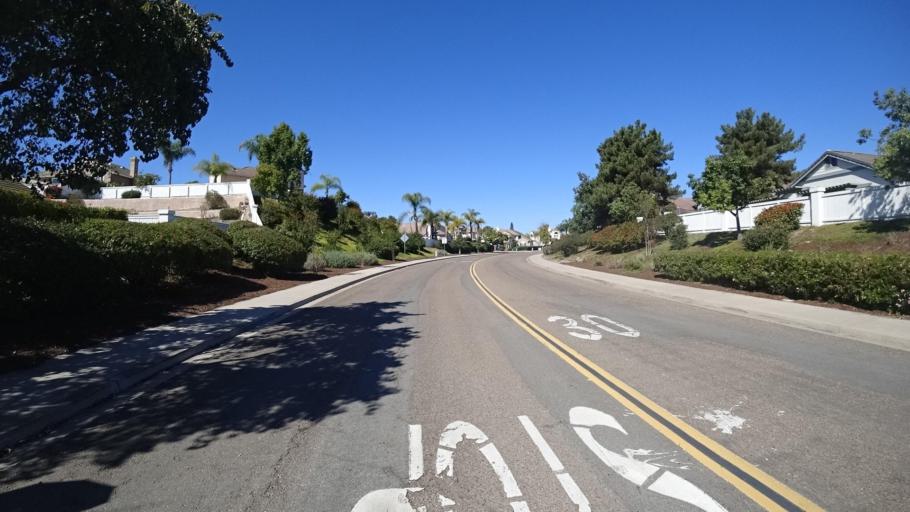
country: US
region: California
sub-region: San Diego County
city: Bonita
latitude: 32.6547
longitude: -116.9860
